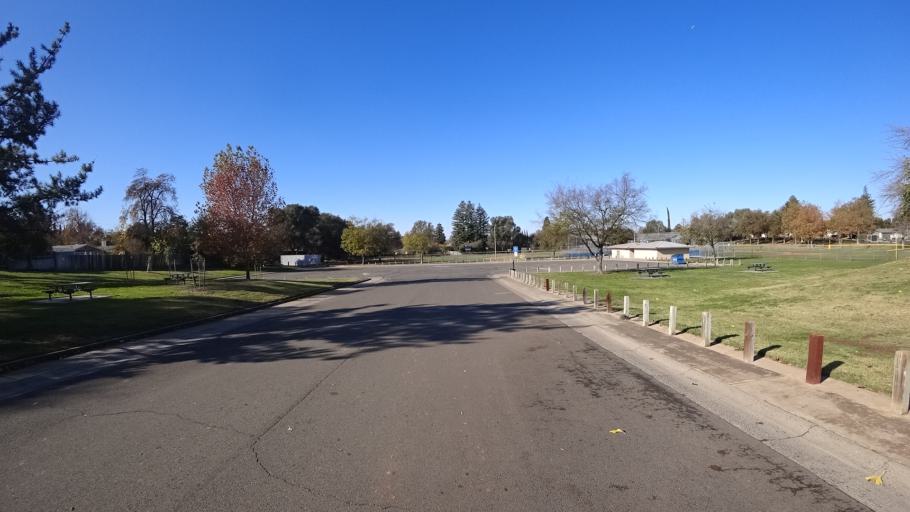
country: US
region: California
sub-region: Sacramento County
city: Fair Oaks
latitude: 38.6712
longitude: -121.3049
